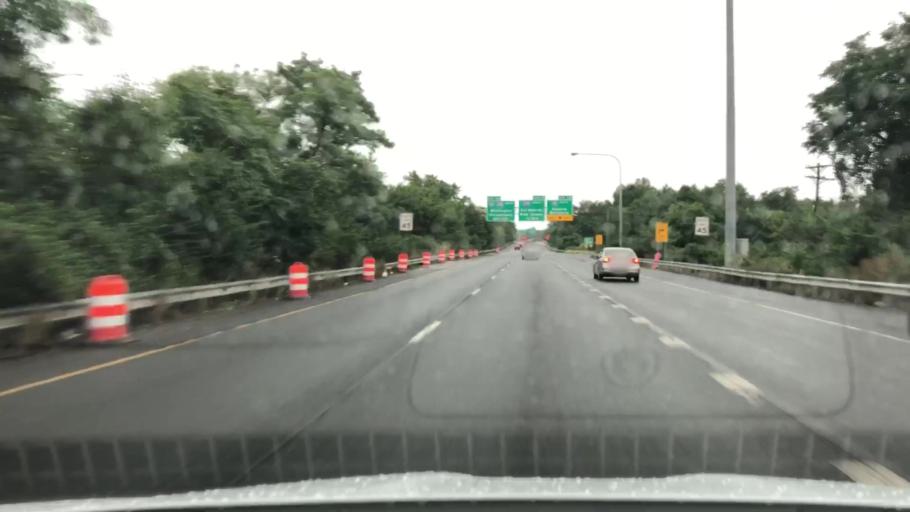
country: US
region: Delaware
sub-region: New Castle County
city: Newport
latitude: 39.7066
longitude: -75.6072
